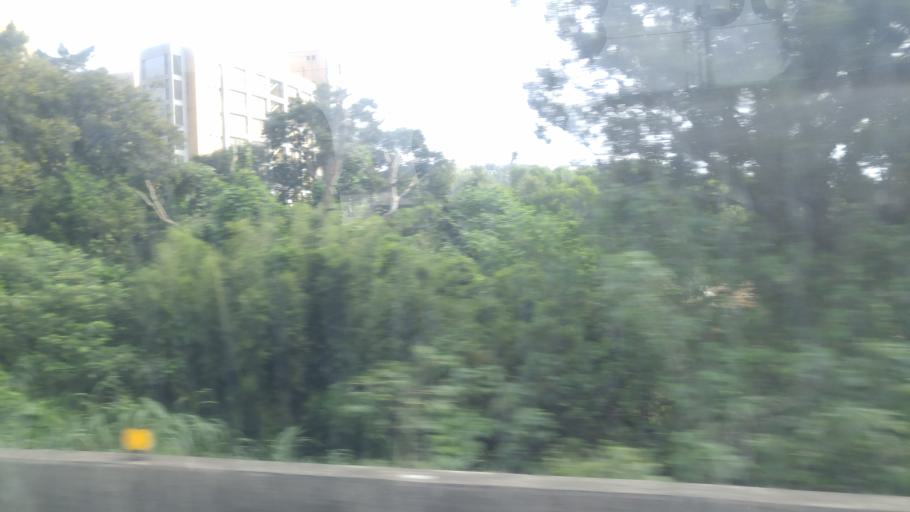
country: TW
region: Taiwan
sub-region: Hsinchu
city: Zhubei
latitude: 24.8957
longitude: 121.1344
